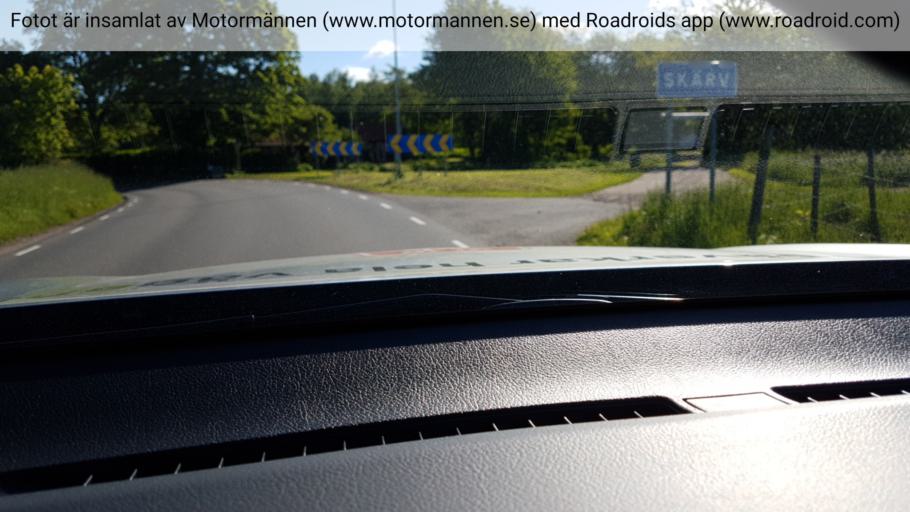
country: SE
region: Vaestra Goetaland
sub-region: Skara Kommun
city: Axvall
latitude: 58.4017
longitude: 13.5977
